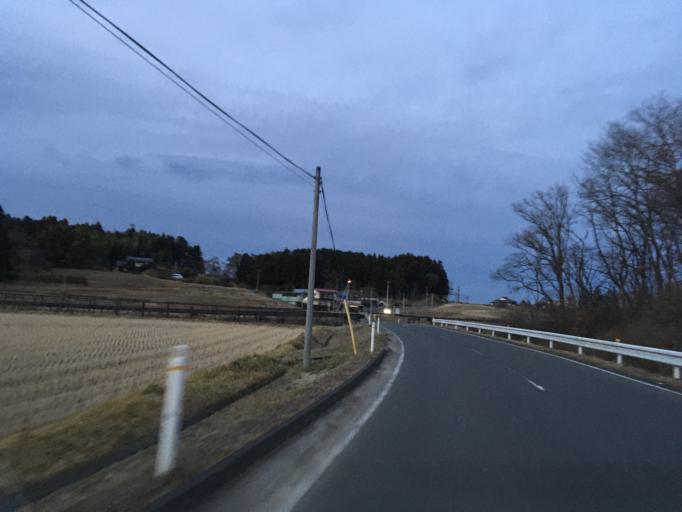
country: JP
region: Miyagi
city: Kogota
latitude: 38.6779
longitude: 141.0923
